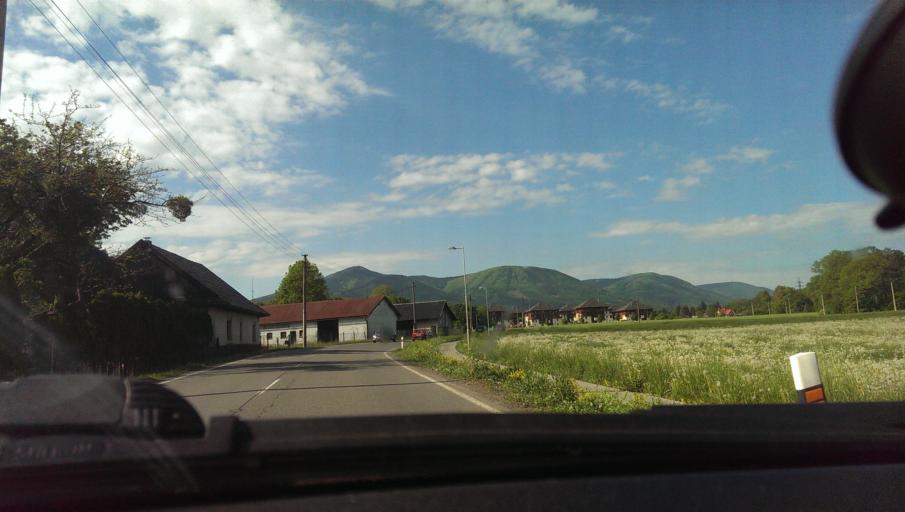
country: CZ
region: Moravskoslezsky
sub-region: Okres Frydek-Mistek
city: Celadna
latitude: 49.5564
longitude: 18.3448
